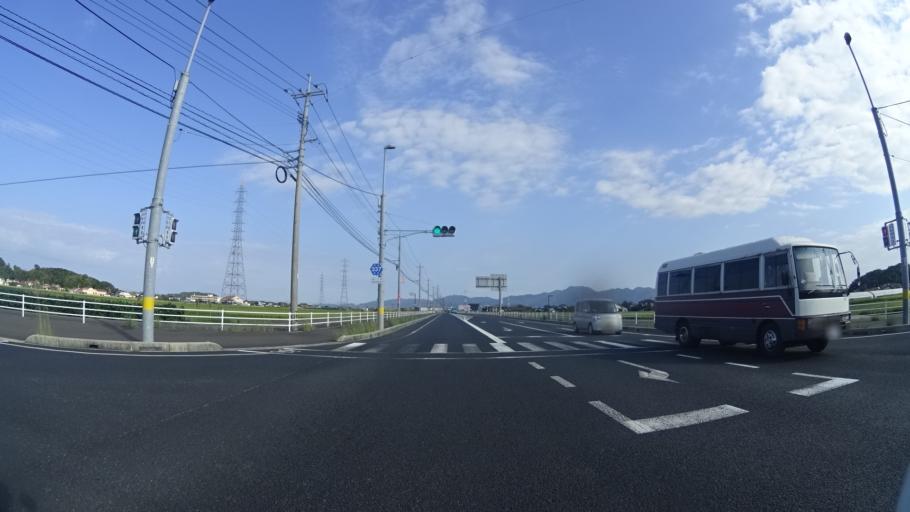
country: JP
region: Shimane
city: Izumo
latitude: 35.3296
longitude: 132.7042
